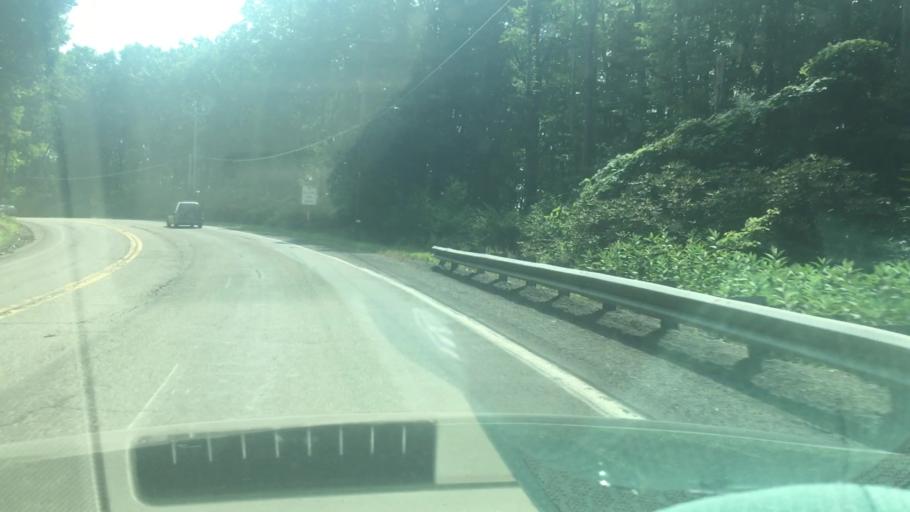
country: US
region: Pennsylvania
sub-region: Schuylkill County
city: Hometown
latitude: 40.8210
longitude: -75.9989
